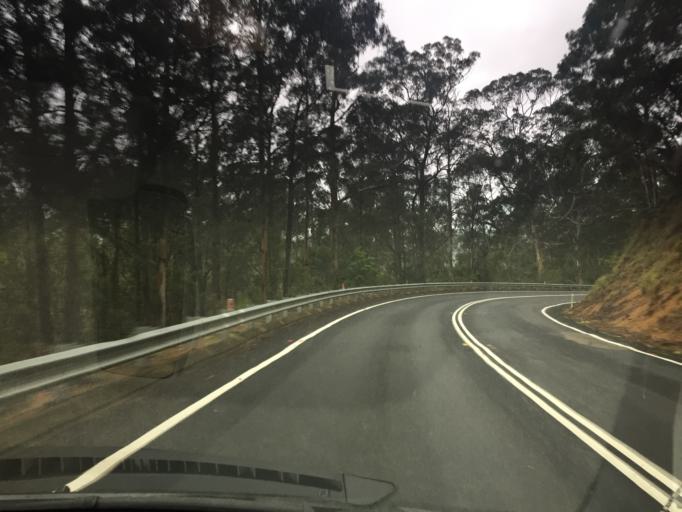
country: AU
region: New South Wales
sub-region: Bega Valley
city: Bega
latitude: -36.6109
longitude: 149.4708
